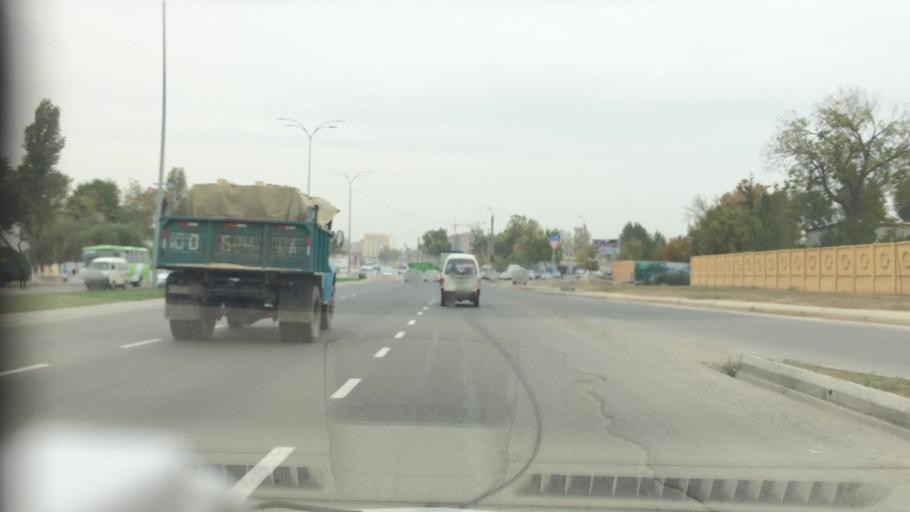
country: UZ
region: Toshkent
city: Salor
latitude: 41.3029
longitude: 69.3436
